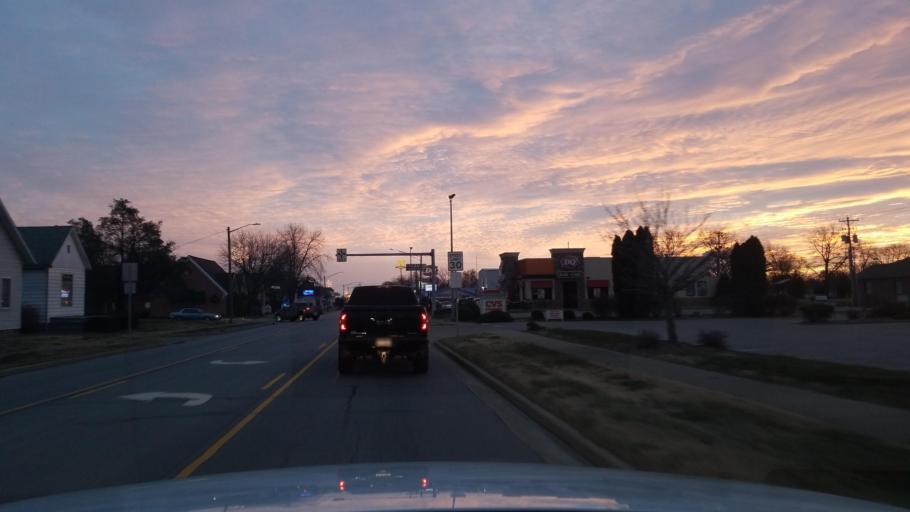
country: US
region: Indiana
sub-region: Posey County
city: Mount Vernon
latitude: 37.9341
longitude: -87.8883
